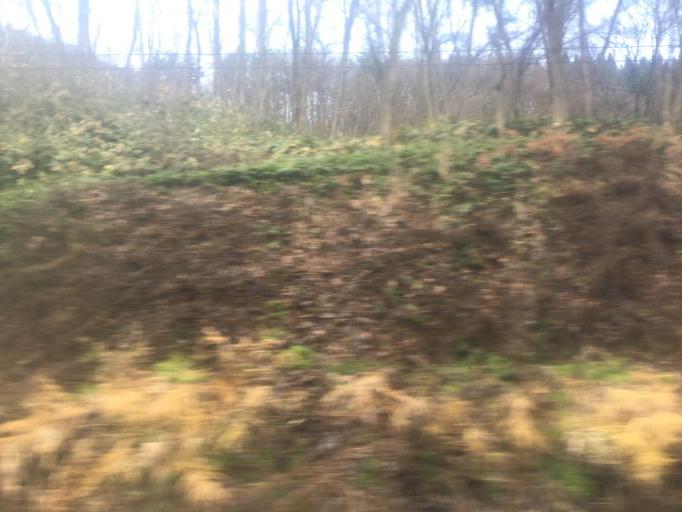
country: JP
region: Akita
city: Takanosu
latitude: 40.2621
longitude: 140.4084
